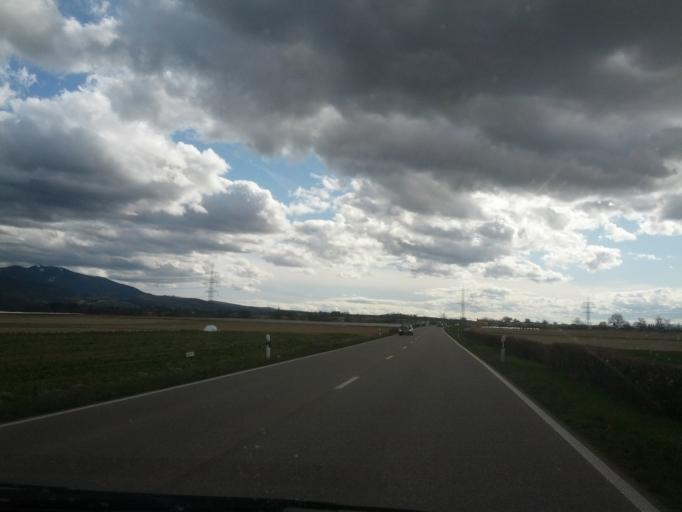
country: DE
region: Baden-Wuerttemberg
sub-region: Freiburg Region
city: Eschbach
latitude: 47.8935
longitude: 7.6722
